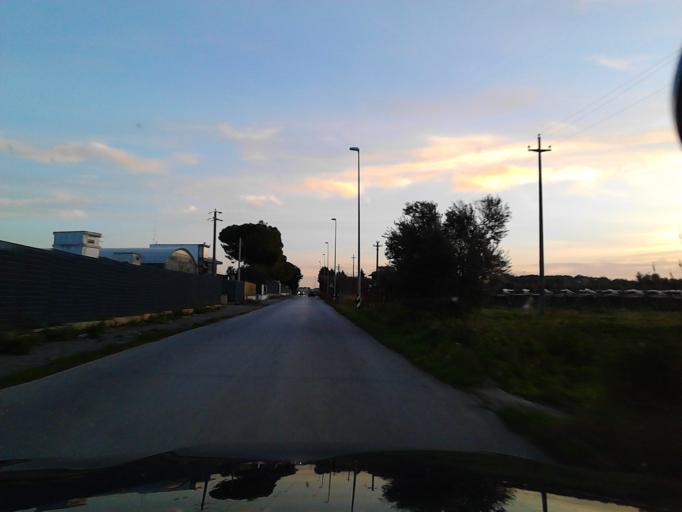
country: IT
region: Apulia
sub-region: Provincia di Bari
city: Adelfia
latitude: 41.0181
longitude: 16.8608
